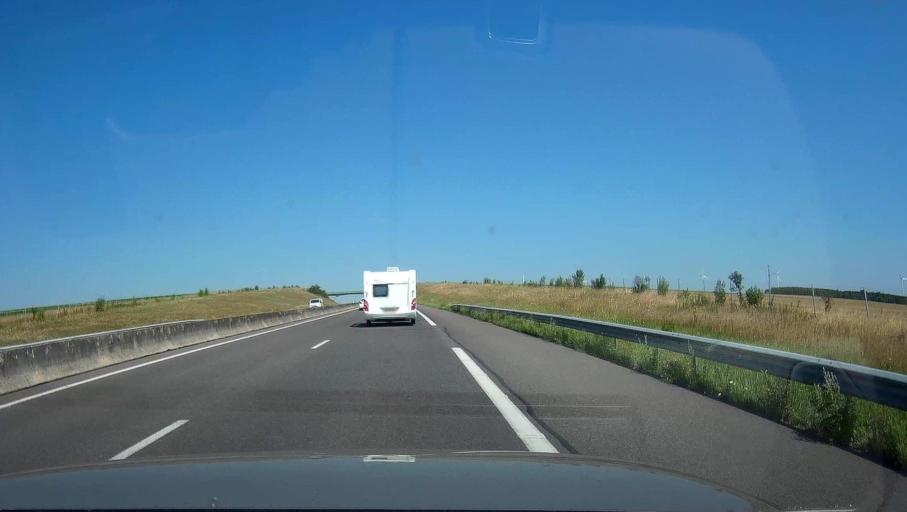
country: FR
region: Champagne-Ardenne
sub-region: Departement de l'Aube
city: Arcis-sur-Aube
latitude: 48.5524
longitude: 4.1930
